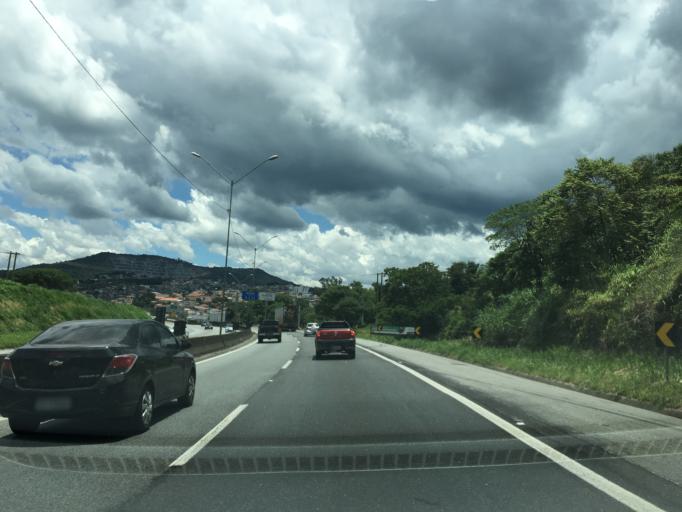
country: BR
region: Sao Paulo
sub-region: Mairipora
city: Mairipora
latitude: -23.3112
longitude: -46.5818
